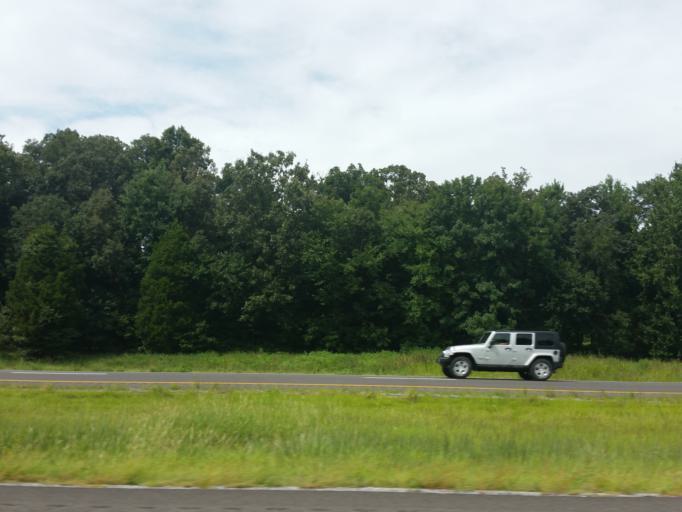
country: US
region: Kentucky
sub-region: Marshall County
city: Calvert City
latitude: 36.9909
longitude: -88.3892
